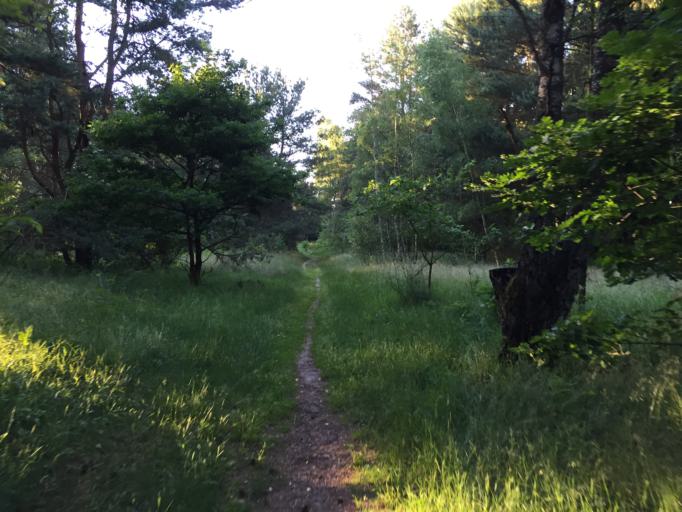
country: SE
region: Skane
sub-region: Lunds Kommun
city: Veberod
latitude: 55.6253
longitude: 13.4934
